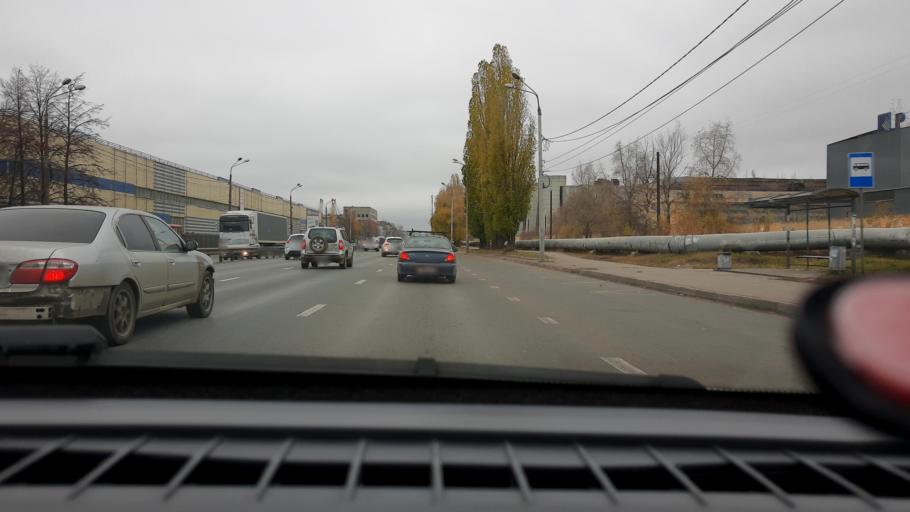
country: RU
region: Nizjnij Novgorod
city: Nizhniy Novgorod
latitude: 56.2607
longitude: 43.9257
